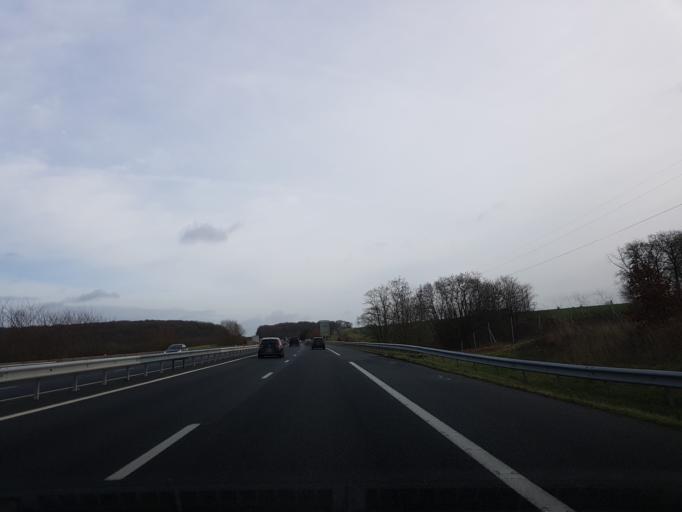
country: FR
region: Bourgogne
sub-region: Departement de l'Yonne
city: Thorigny-sur-Oreuse
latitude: 48.2356
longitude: 3.4377
